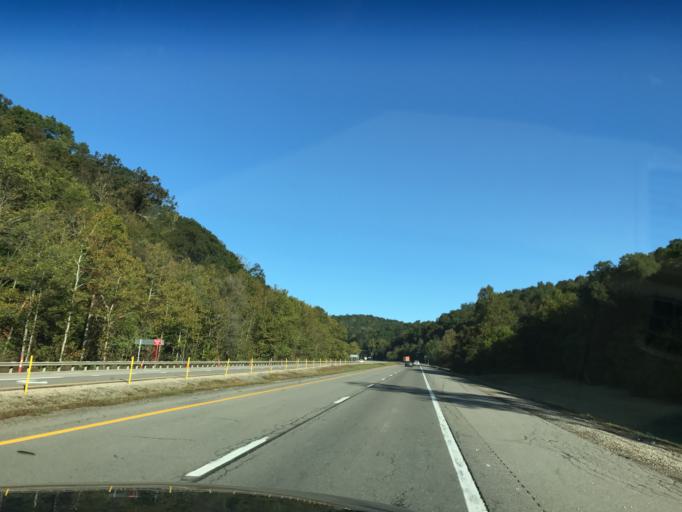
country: US
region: Ohio
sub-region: Washington County
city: Newport
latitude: 39.2422
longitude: -81.2290
